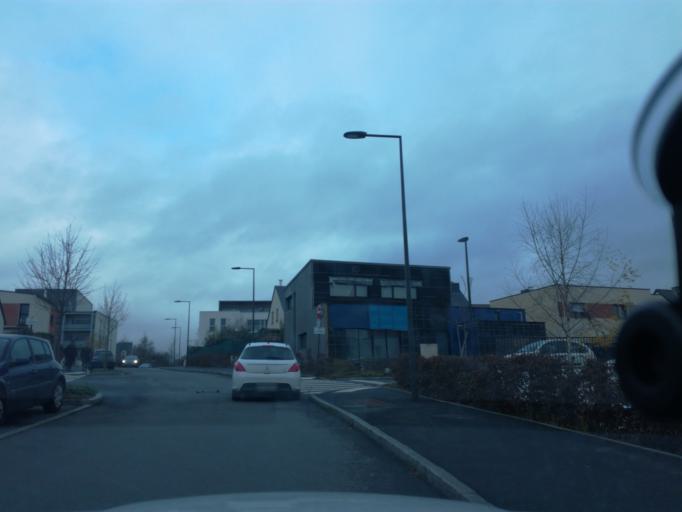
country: FR
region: Brittany
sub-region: Departement d'Ille-et-Vilaine
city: Fouillard
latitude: 48.1503
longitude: -1.5811
